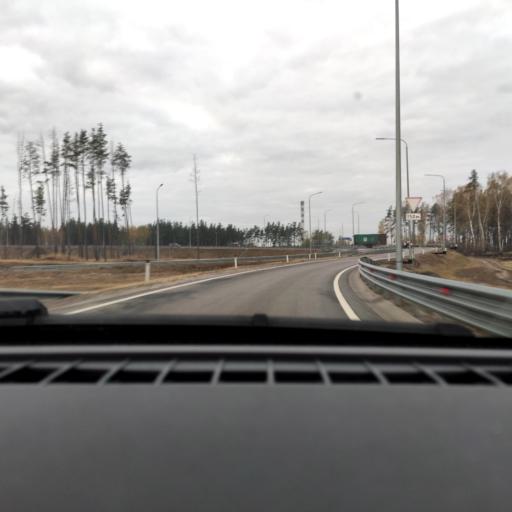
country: RU
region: Voronezj
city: Somovo
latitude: 51.7436
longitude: 39.3063
